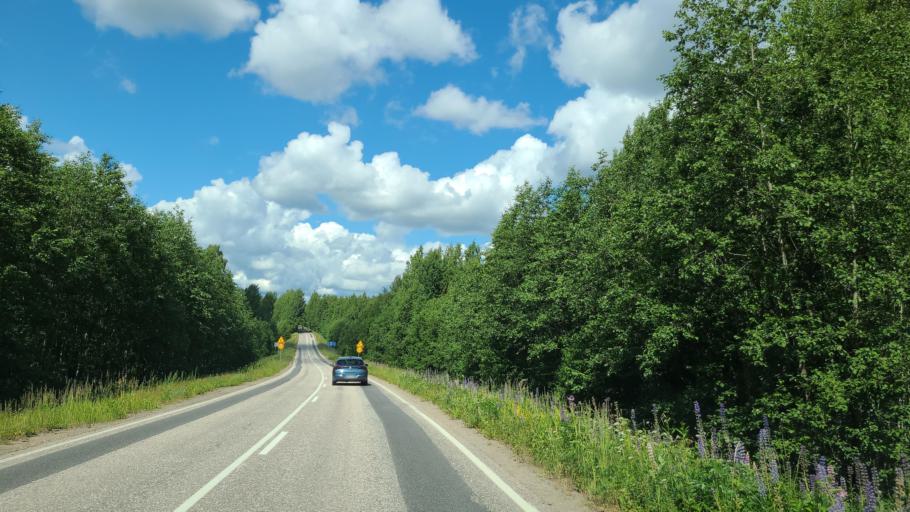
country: FI
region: Northern Savo
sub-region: Koillis-Savo
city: Kaavi
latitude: 62.9205
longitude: 28.6982
